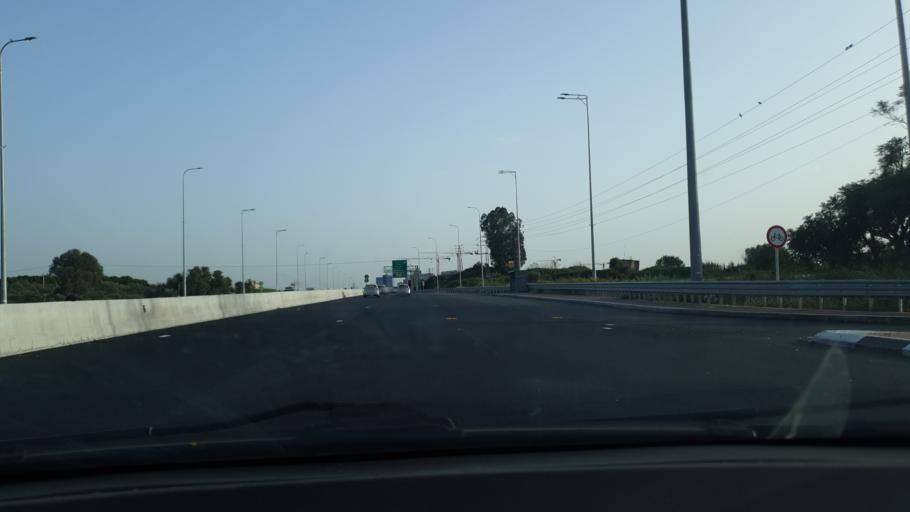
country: IL
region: Central District
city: Ra'anana
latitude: 32.2100
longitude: 34.8837
